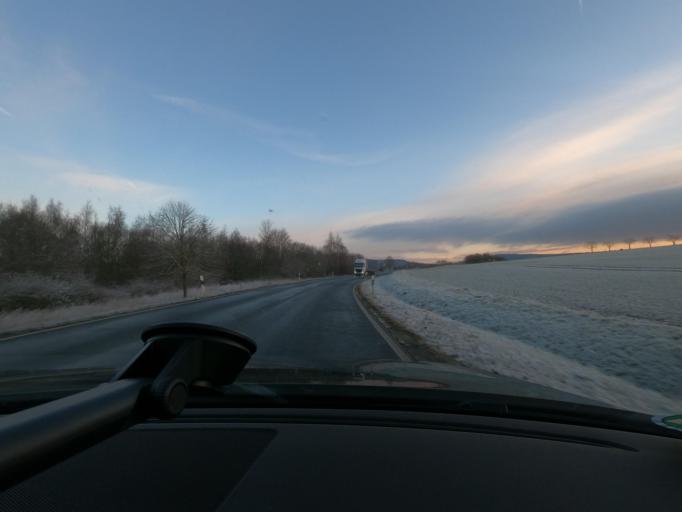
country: DE
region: Thuringia
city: Breitenworbis
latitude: 51.4068
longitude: 10.4341
